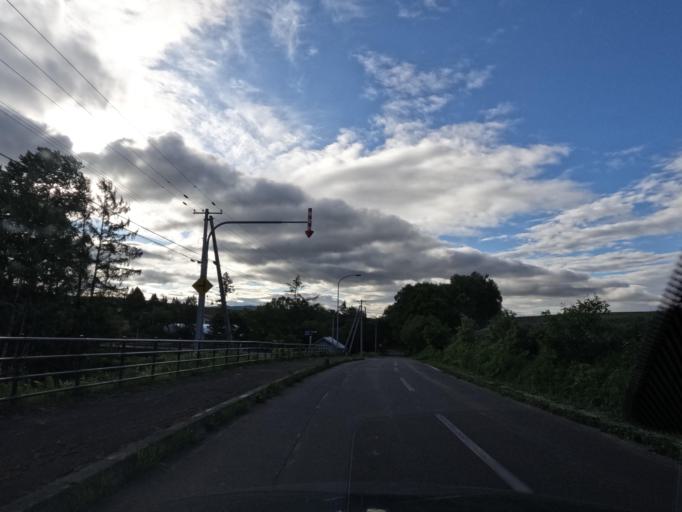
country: JP
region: Hokkaido
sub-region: Asahikawa-shi
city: Asahikawa
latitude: 43.6314
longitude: 142.4351
